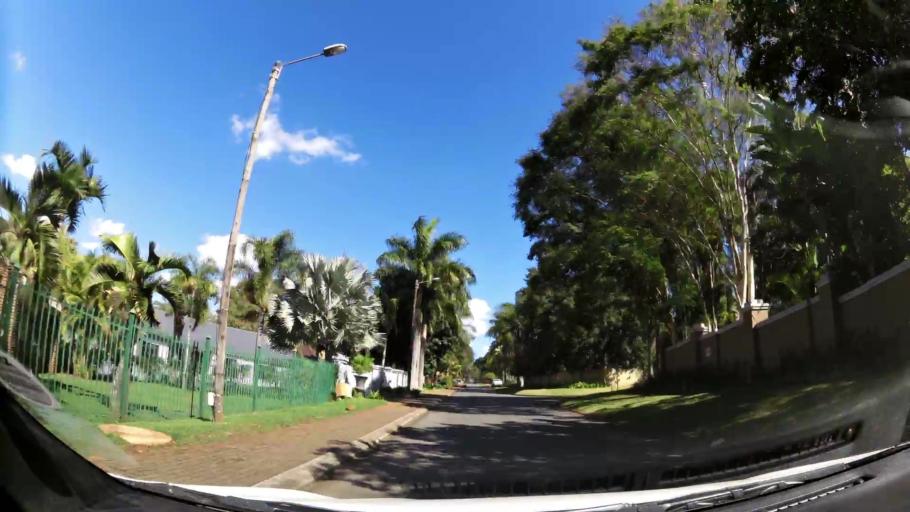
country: ZA
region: Limpopo
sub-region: Mopani District Municipality
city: Tzaneen
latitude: -23.8207
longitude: 30.1483
